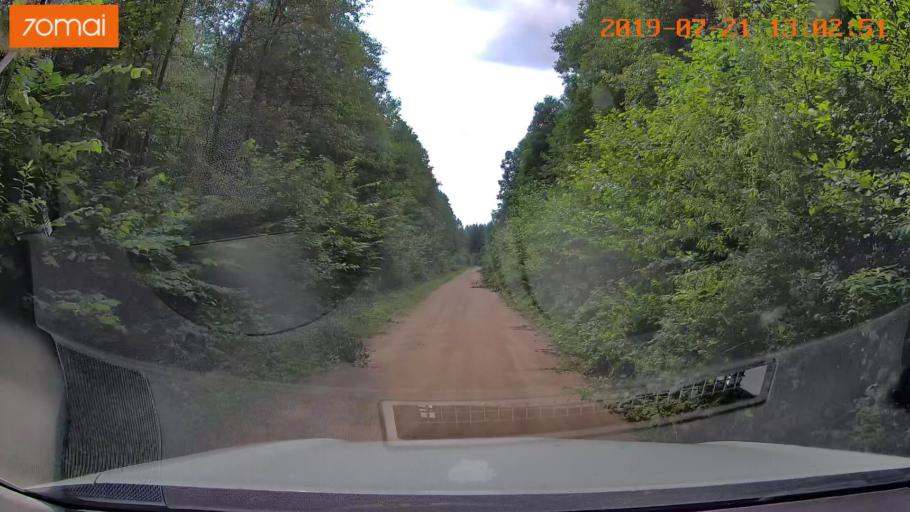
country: BY
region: Grodnenskaya
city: Lyubcha
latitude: 53.8456
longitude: 26.0245
